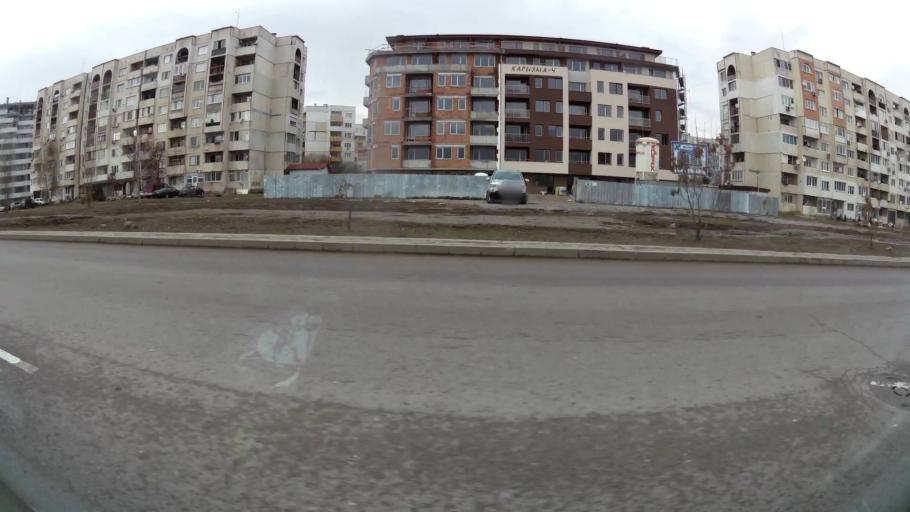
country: BG
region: Sofia-Capital
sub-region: Stolichna Obshtina
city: Sofia
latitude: 42.7359
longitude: 23.2715
